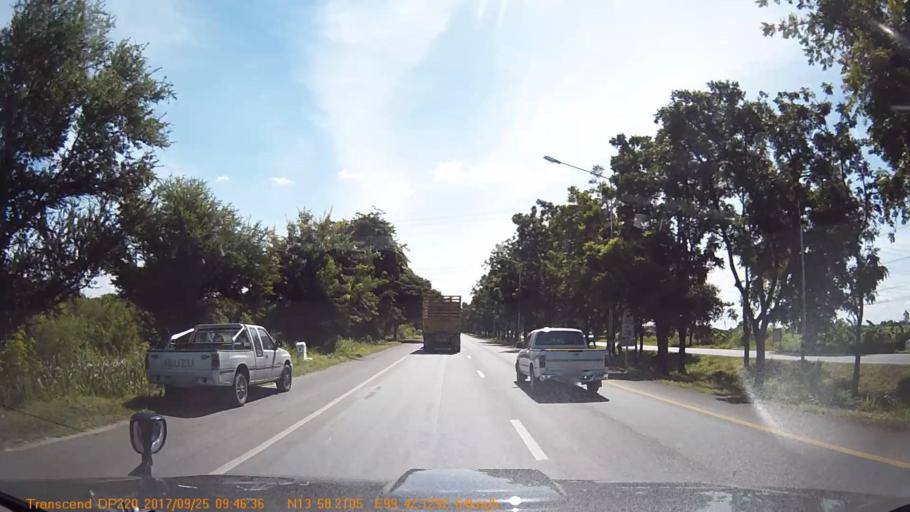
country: TH
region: Kanchanaburi
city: Tha Muang
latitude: 13.9701
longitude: 99.7026
